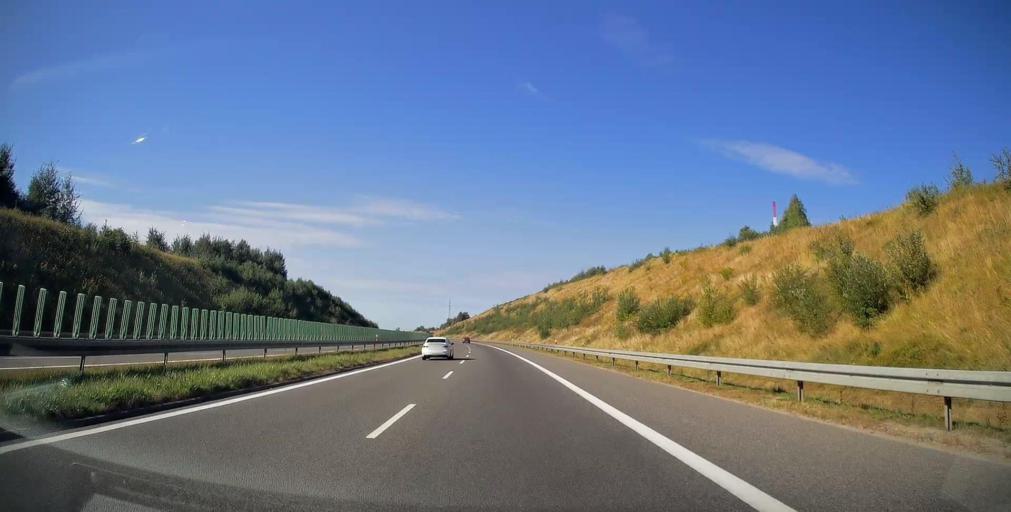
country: PL
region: Swietokrzyskie
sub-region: Powiat skarzyski
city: Laczna
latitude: 50.9837
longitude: 20.7541
